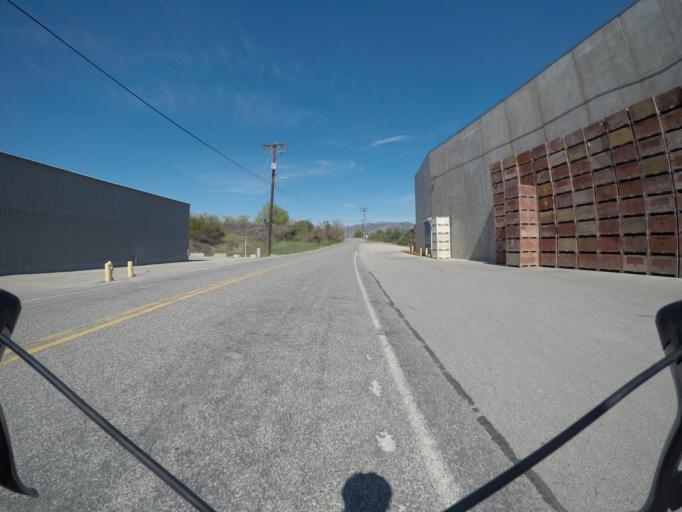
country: US
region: Washington
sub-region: Chelan County
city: Cashmere
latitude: 47.4881
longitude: -120.4201
